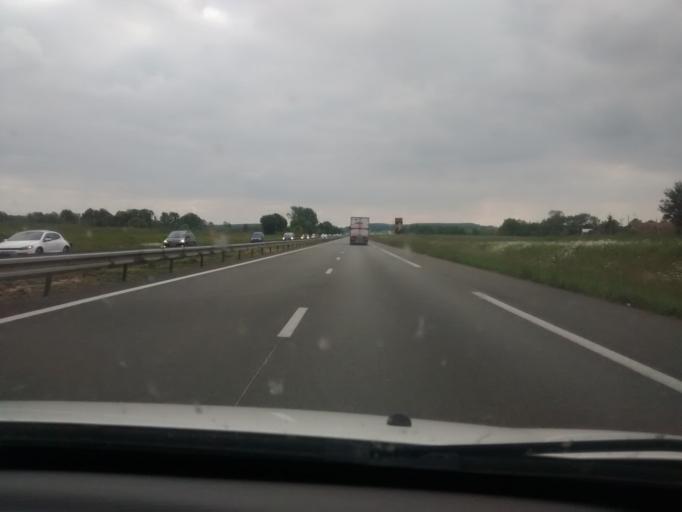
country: FR
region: Pays de la Loire
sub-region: Departement de la Sarthe
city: Coulans-sur-Gee
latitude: 48.0177
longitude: -0.0531
